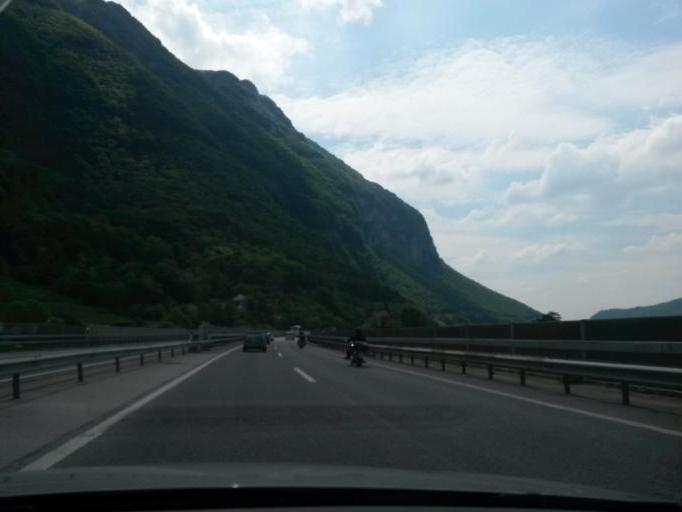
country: CH
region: Ticino
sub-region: Lugano District
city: Melano
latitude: 45.9188
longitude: 8.9842
